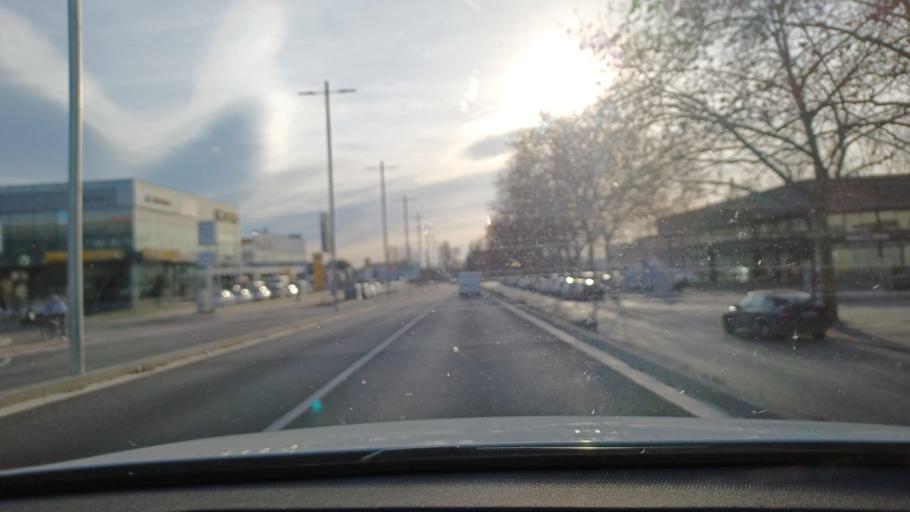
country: ES
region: Catalonia
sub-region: Provincia de Barcelona
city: Vilafranca del Penedes
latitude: 41.3366
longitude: 1.6871
